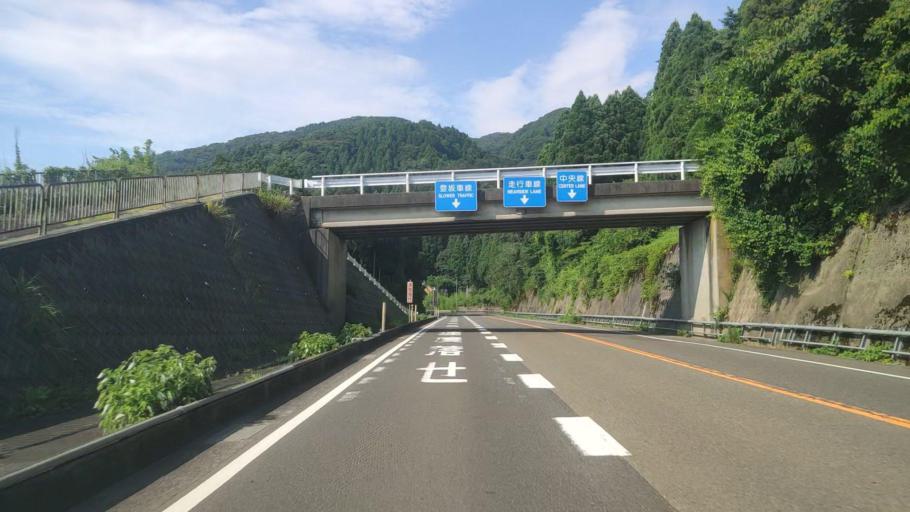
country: JP
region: Fukui
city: Tsuruga
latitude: 35.7549
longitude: 136.1053
